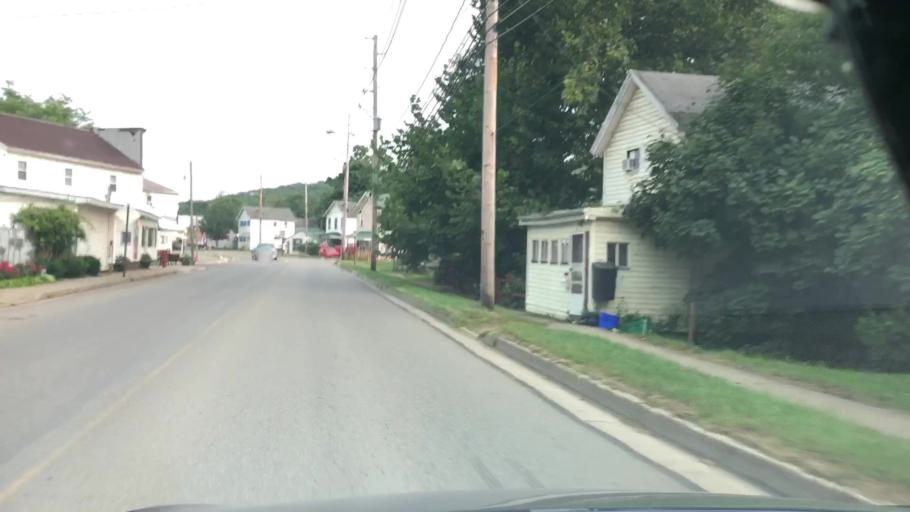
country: US
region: Pennsylvania
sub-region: Crawford County
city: Titusville
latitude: 41.6300
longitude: -79.6856
